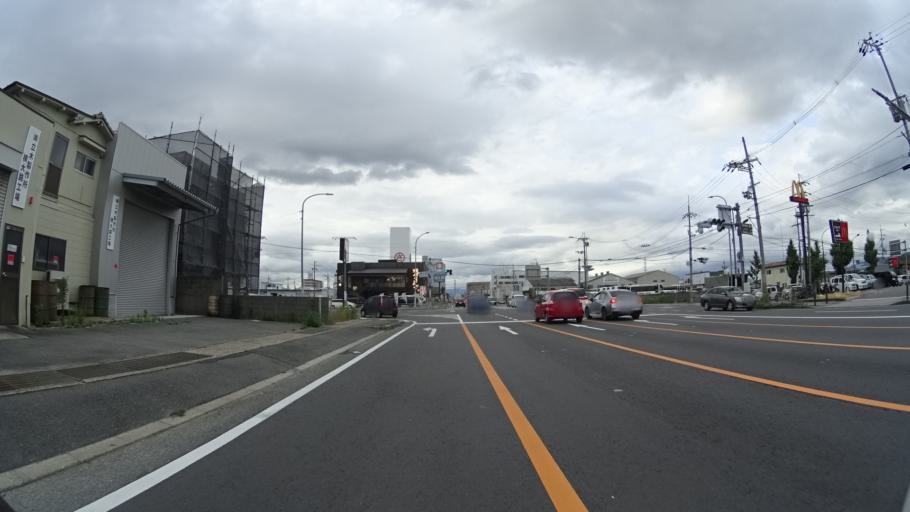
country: JP
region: Kyoto
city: Muko
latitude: 34.9263
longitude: 135.7447
